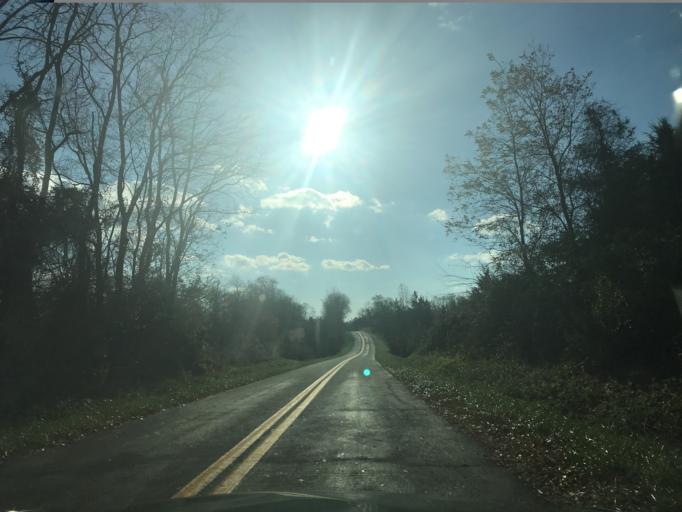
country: US
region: Maryland
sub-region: Carroll County
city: New Windsor
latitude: 39.6244
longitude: -77.0980
